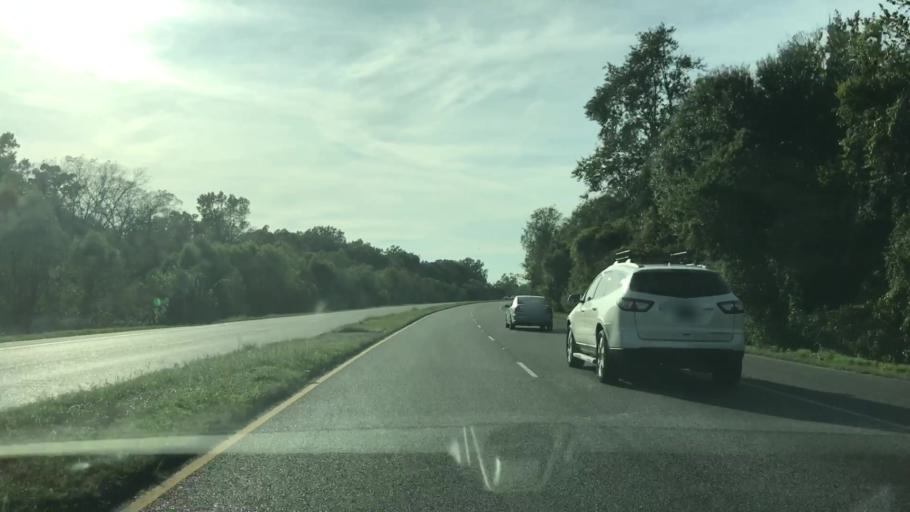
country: US
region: Louisiana
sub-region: Jefferson Parish
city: Avondale
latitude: 29.9097
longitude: -90.1840
